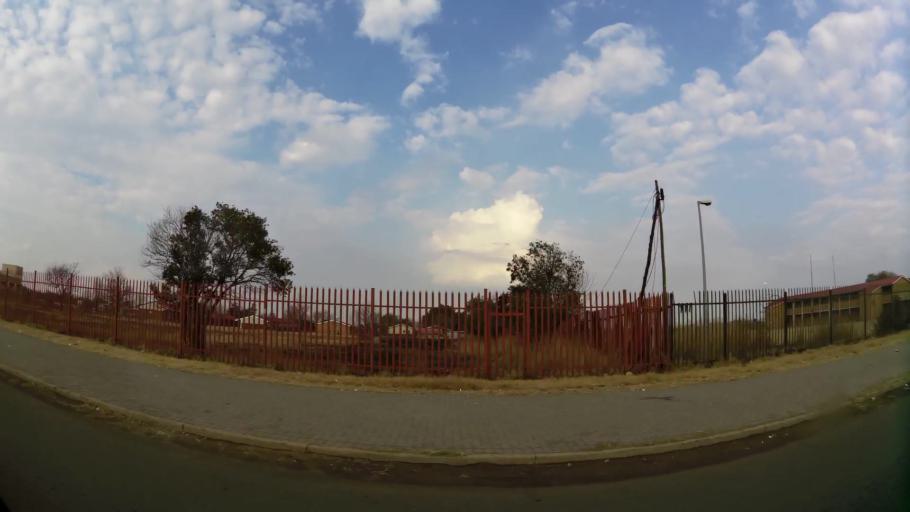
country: ZA
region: Gauteng
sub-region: Sedibeng District Municipality
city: Vanderbijlpark
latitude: -26.6890
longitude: 27.8678
